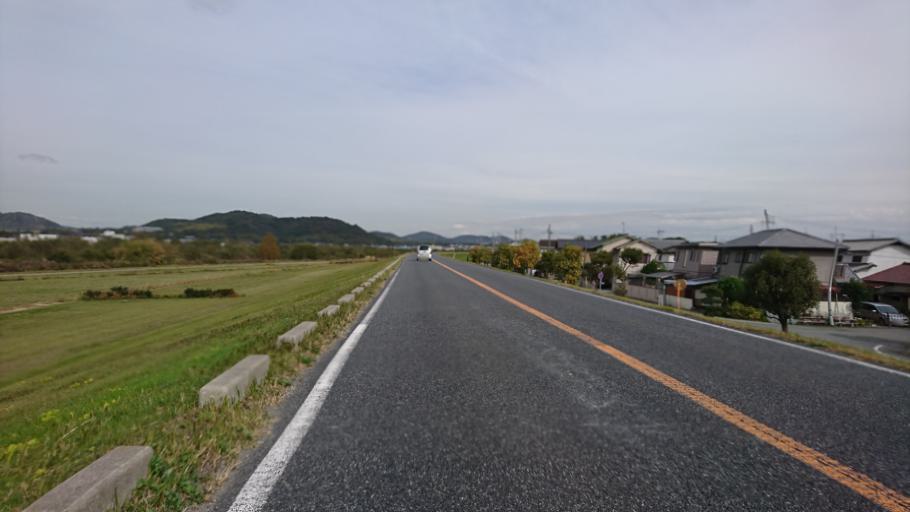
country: JP
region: Hyogo
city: Kakogawacho-honmachi
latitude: 34.7906
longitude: 134.8701
